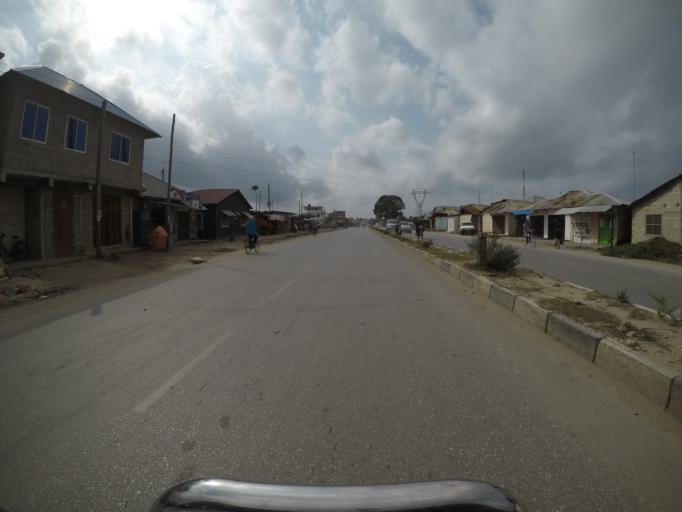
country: TZ
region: Zanzibar Urban/West
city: Zanzibar
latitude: -6.1847
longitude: 39.2353
